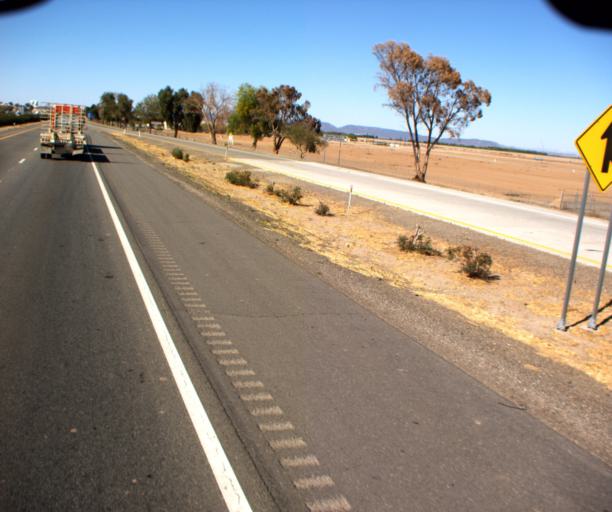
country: US
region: Arizona
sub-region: Yuma County
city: Yuma
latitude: 32.7104
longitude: -114.6109
